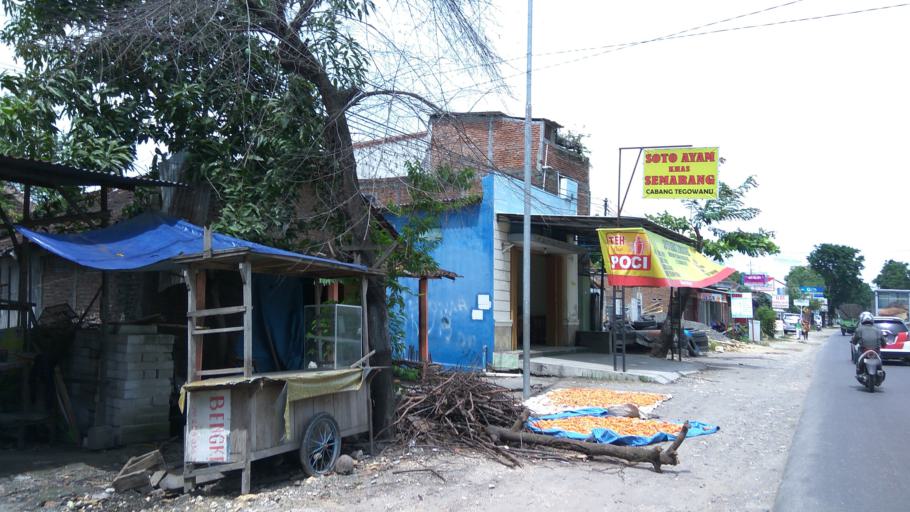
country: ID
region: Central Java
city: Mranggen
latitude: -7.0510
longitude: 110.6557
